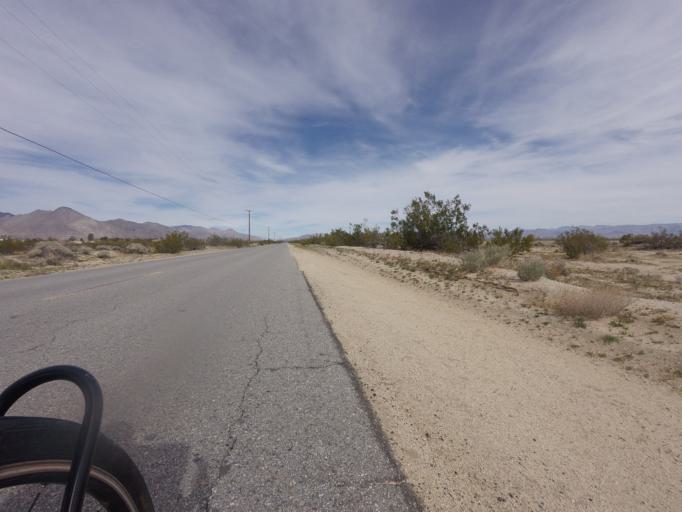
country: US
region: California
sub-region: Kern County
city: Inyokern
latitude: 35.7327
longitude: -117.8378
